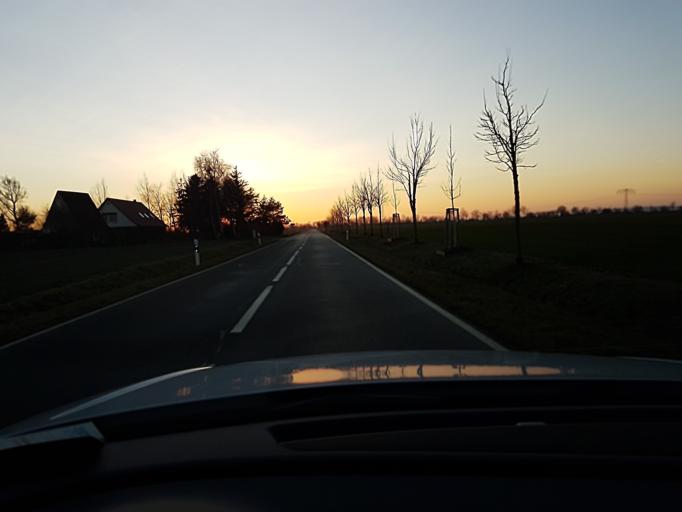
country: DE
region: Mecklenburg-Vorpommern
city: Wiek
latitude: 54.5678
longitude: 13.2564
